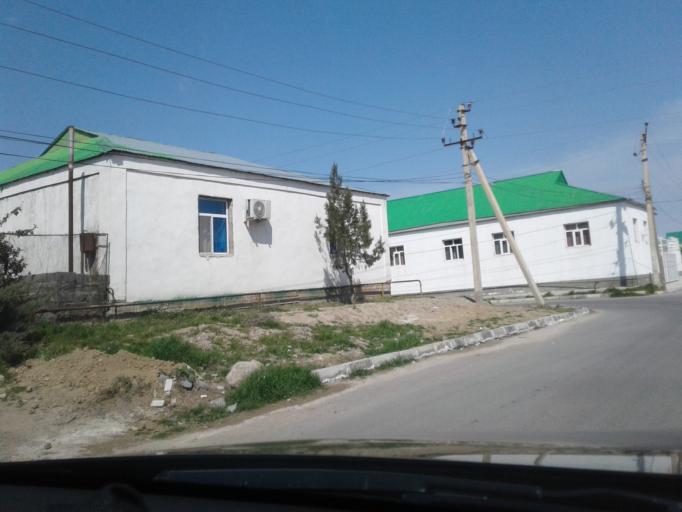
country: TM
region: Ahal
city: Ashgabat
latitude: 37.9857
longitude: 58.3952
